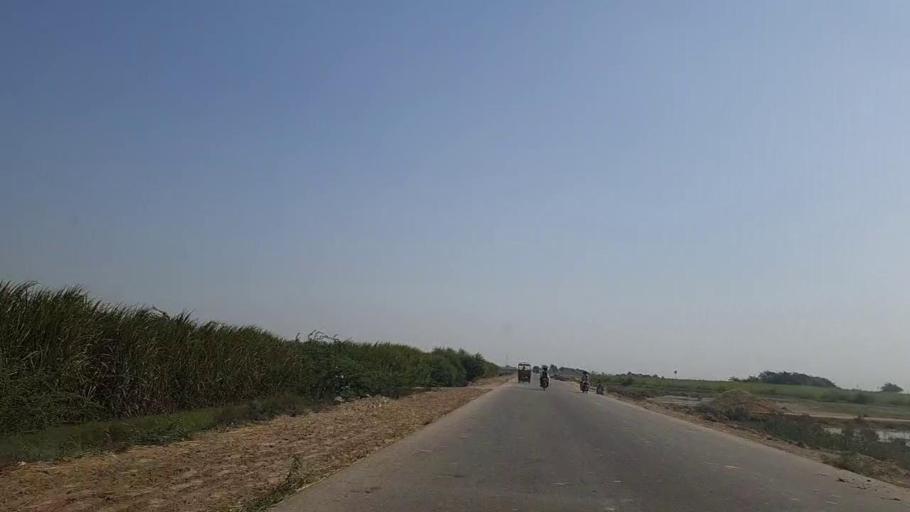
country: PK
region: Sindh
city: Mirpur Batoro
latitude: 24.7545
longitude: 68.2300
